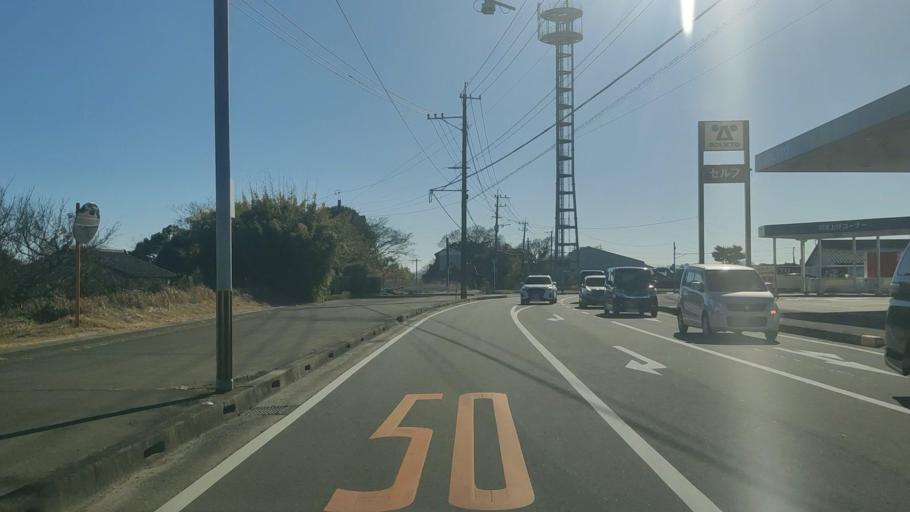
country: JP
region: Miyazaki
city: Miyazaki-shi
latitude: 31.9559
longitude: 131.4629
